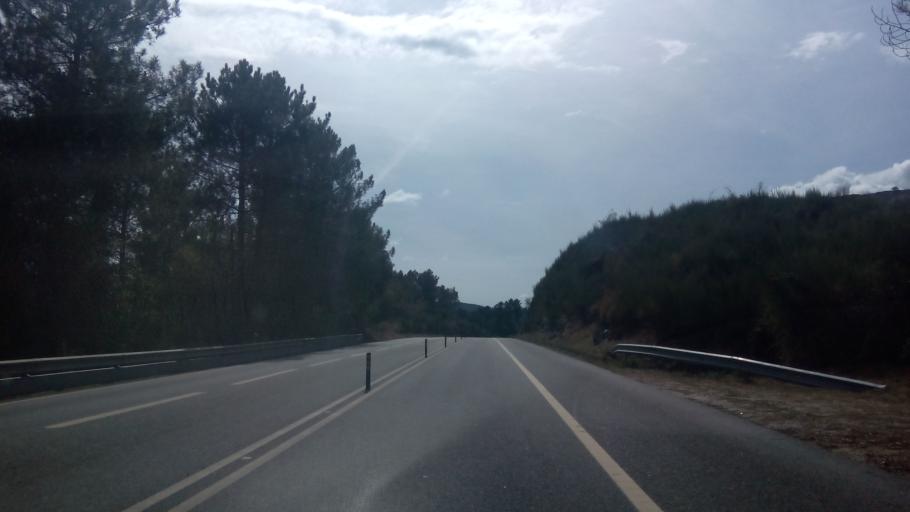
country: PT
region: Porto
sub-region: Amarante
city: Amarante
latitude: 41.2694
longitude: -8.0163
